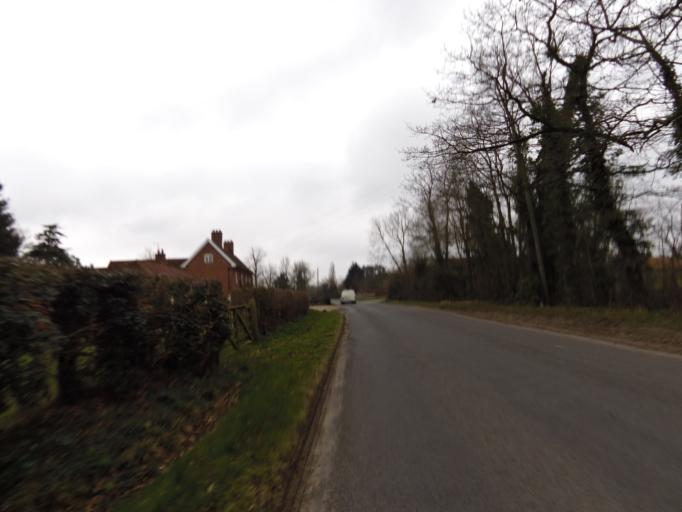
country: GB
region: England
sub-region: Suffolk
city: Framlingham
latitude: 52.1981
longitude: 1.3246
